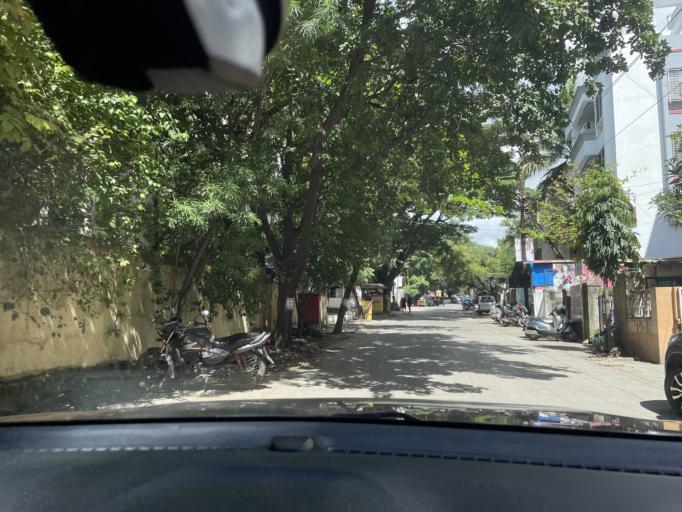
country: IN
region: Maharashtra
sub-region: Pune Division
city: Shivaji Nagar
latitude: 18.5154
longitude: 73.7798
